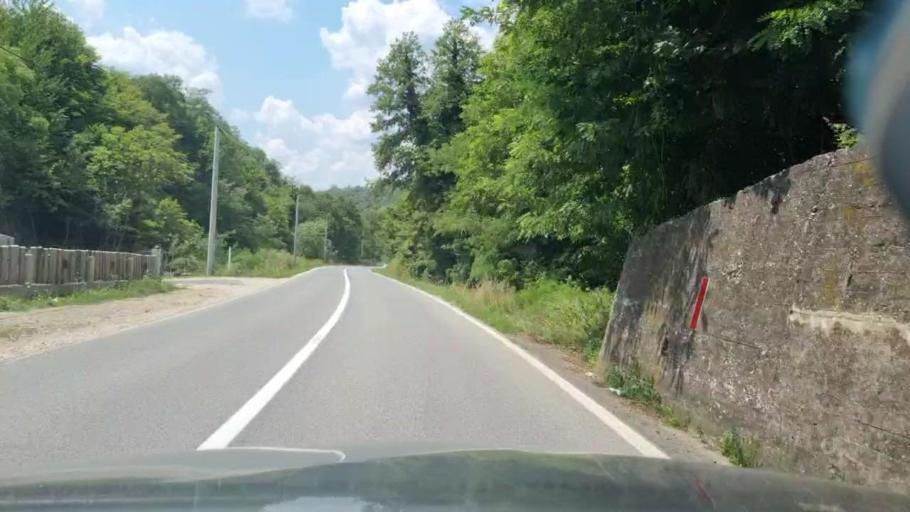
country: BA
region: Federation of Bosnia and Herzegovina
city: Tojsici
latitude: 44.5332
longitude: 18.8285
